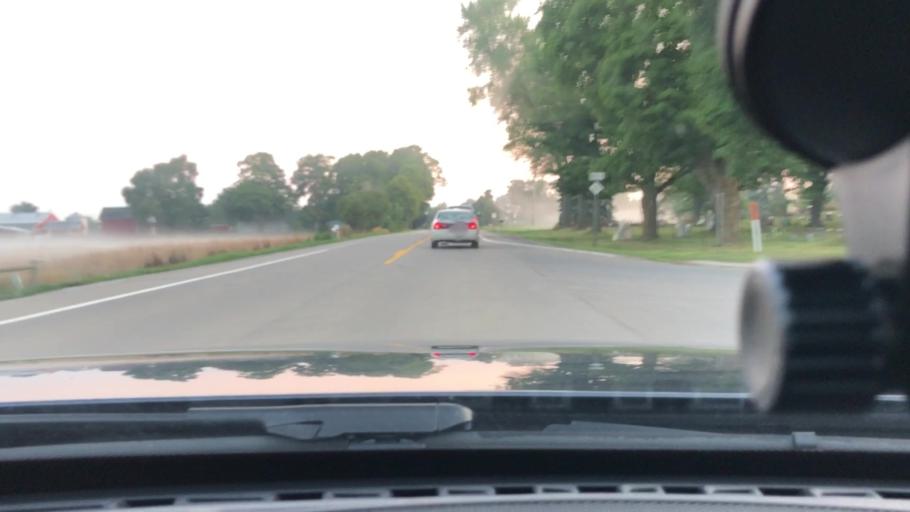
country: US
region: Michigan
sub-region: Washtenaw County
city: Chelsea
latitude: 42.2802
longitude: -84.0315
